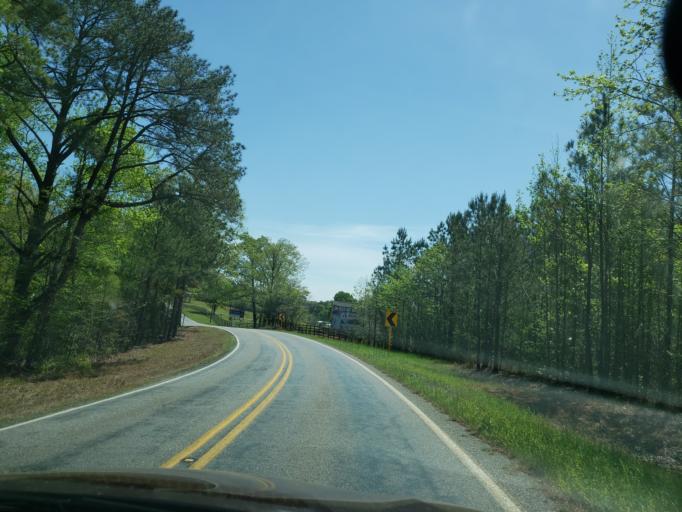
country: US
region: Alabama
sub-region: Tallapoosa County
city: Dadeville
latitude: 32.7055
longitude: -85.8177
